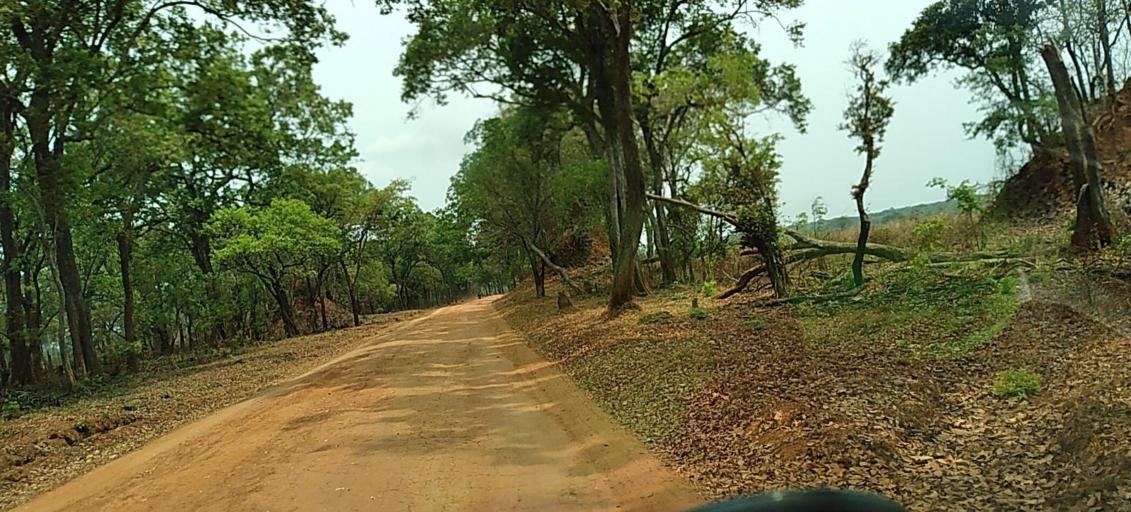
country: ZM
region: North-Western
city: Solwezi
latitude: -12.8133
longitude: 26.5366
